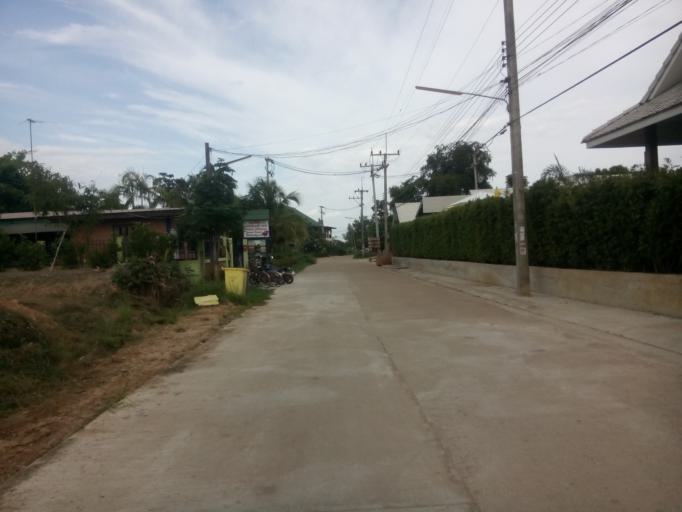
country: TH
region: Sukhothai
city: Ban Na
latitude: 17.0133
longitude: 99.7153
